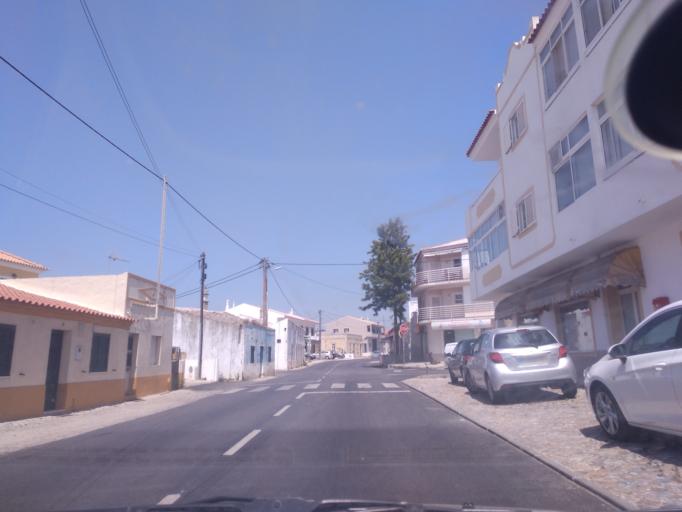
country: PT
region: Faro
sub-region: Faro
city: Faro
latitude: 37.0518
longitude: -7.9515
